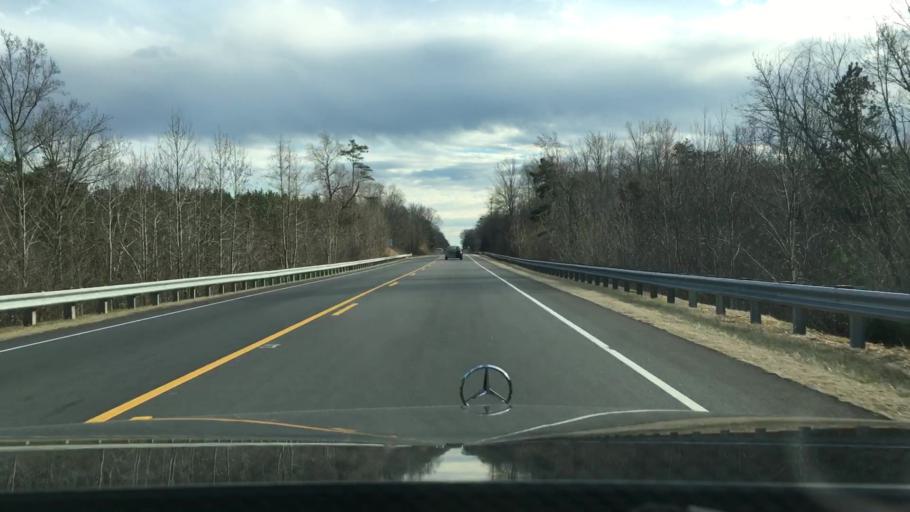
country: US
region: Virginia
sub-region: City of Danville
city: Danville
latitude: 36.4993
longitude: -79.3870
